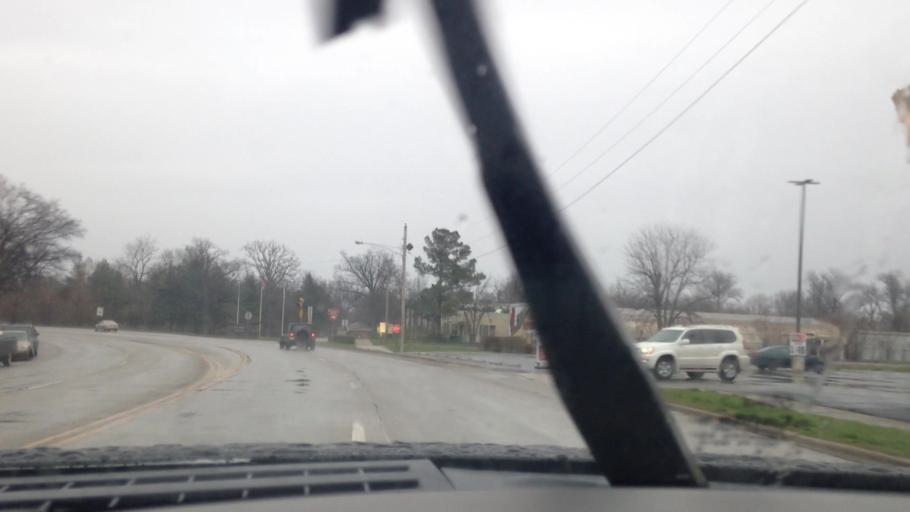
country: US
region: Illinois
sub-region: Massac County
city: Metropolis
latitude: 37.1449
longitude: -88.7163
